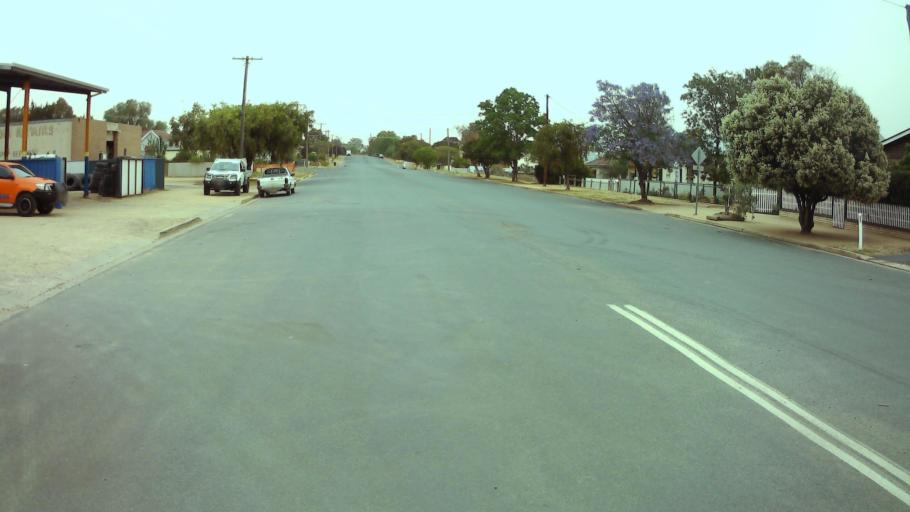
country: AU
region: New South Wales
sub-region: Weddin
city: Grenfell
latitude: -33.8947
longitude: 148.1578
